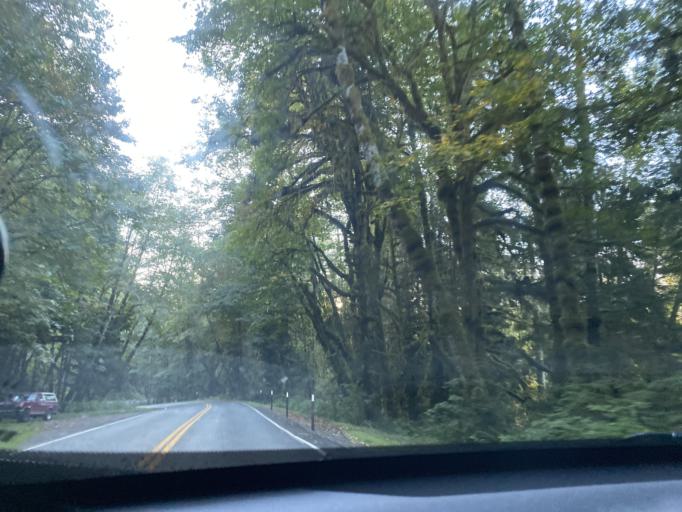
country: US
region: Washington
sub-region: Clallam County
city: Forks
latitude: 47.8238
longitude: -124.2038
